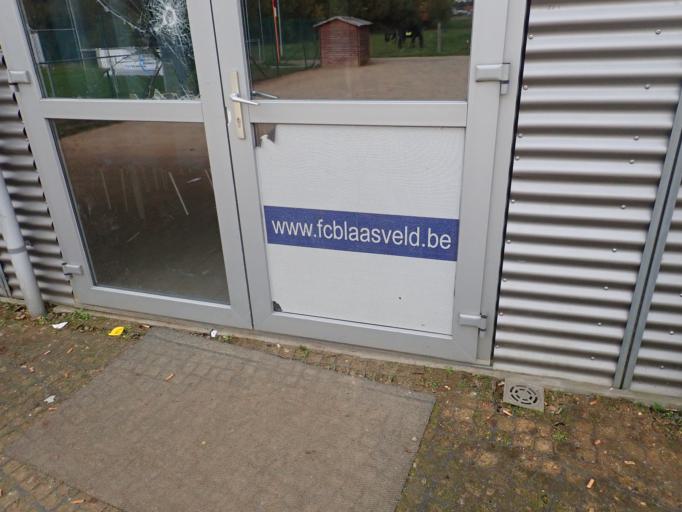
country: BE
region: Flanders
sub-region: Provincie Antwerpen
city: Willebroek
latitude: 51.0600
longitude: 4.3774
